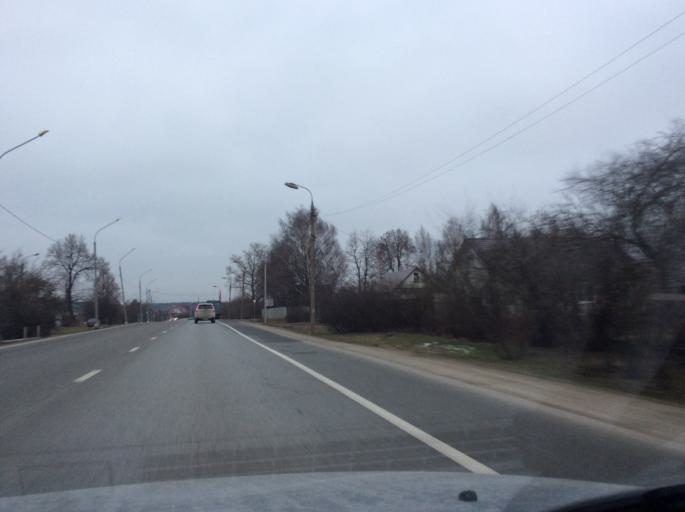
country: RU
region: Moskovskaya
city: Troitsk
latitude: 55.3674
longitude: 37.1999
